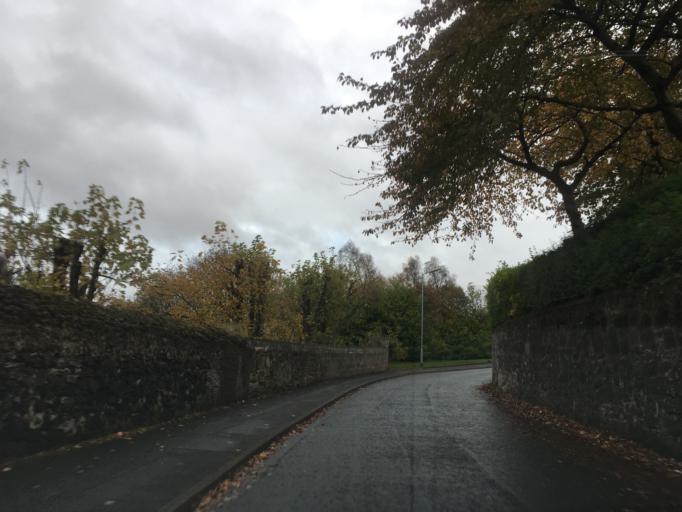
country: GB
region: Scotland
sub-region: Falkirk
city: Bo'ness
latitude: 56.0166
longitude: -3.6037
